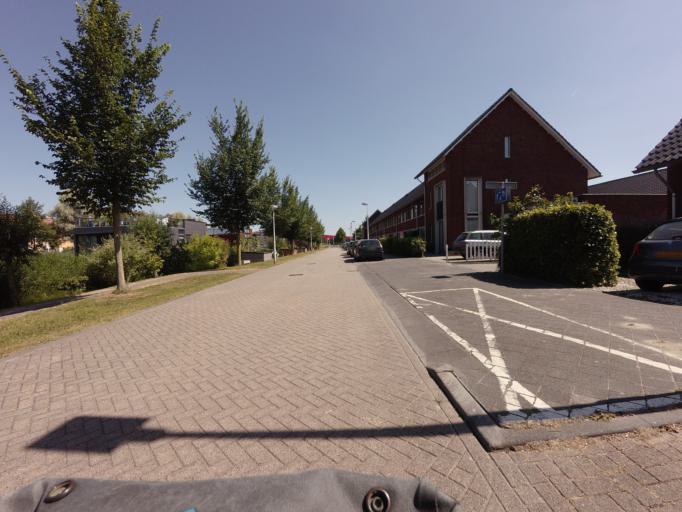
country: NL
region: Utrecht
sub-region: Stichtse Vecht
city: Maarssen
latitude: 52.1048
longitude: 5.0500
